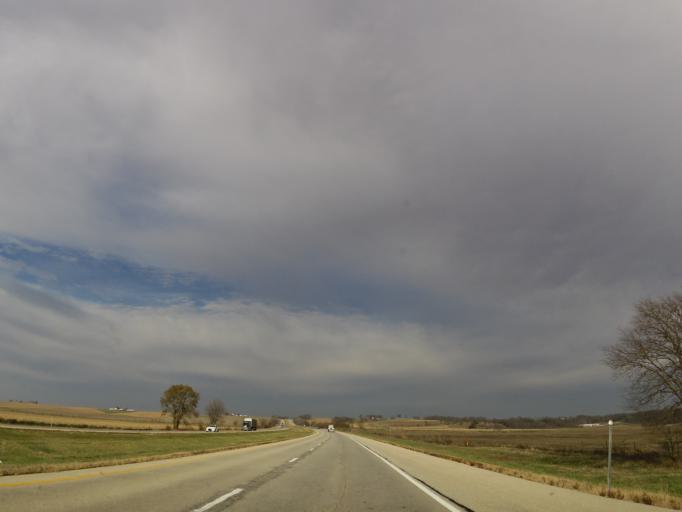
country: US
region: Illinois
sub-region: Henry County
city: Orion
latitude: 41.2603
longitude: -90.3294
